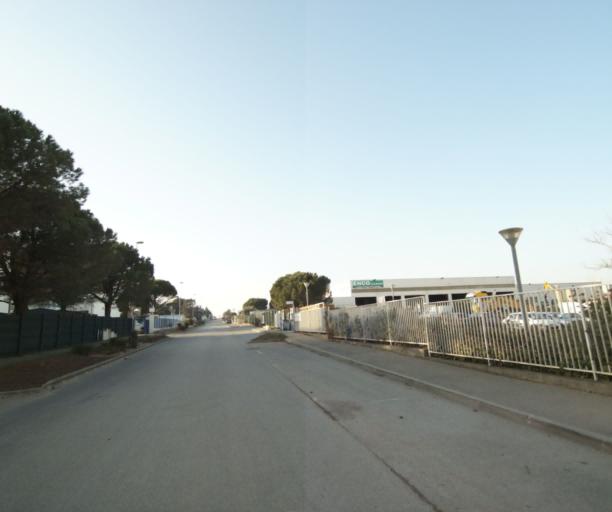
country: FR
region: Provence-Alpes-Cote d'Azur
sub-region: Departement des Bouches-du-Rhone
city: Saint-Victoret
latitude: 43.4267
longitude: 5.2434
